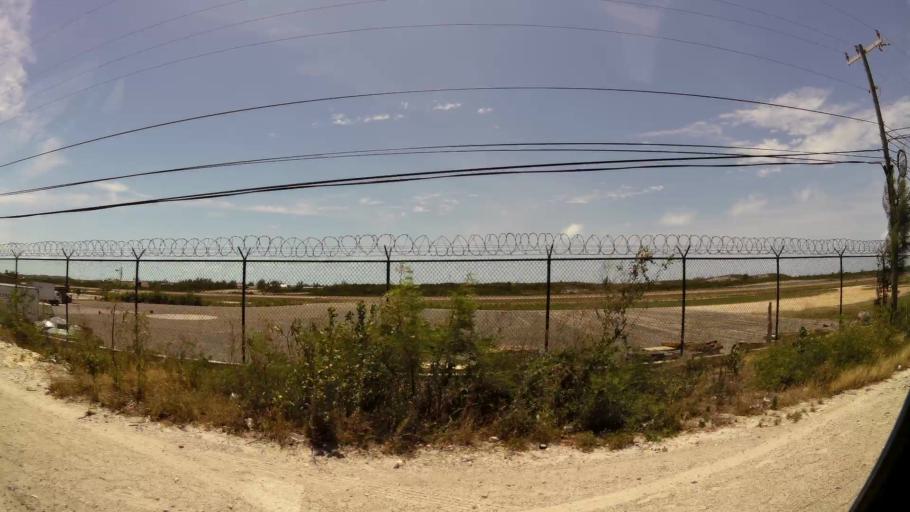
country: BS
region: Mayaguana
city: Abraham's Bay
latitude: 21.7752
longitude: -72.2600
